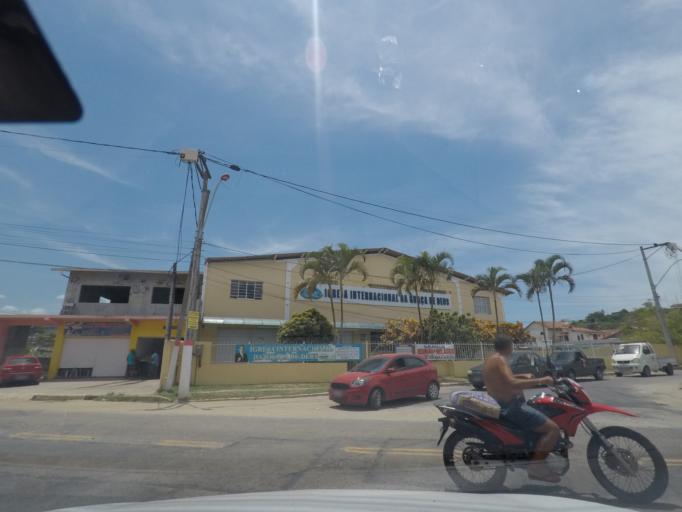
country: BR
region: Rio de Janeiro
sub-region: Marica
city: Marica
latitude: -22.9238
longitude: -42.8184
